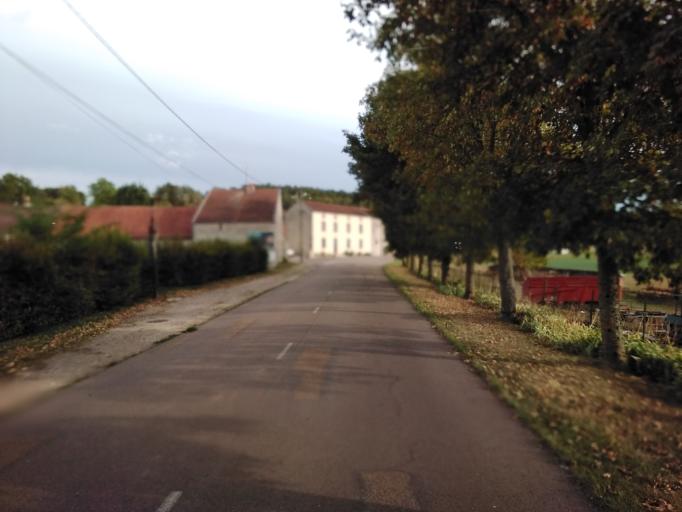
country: FR
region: Champagne-Ardenne
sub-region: Departement de l'Aube
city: Les Riceys
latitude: 47.9154
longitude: 4.3643
